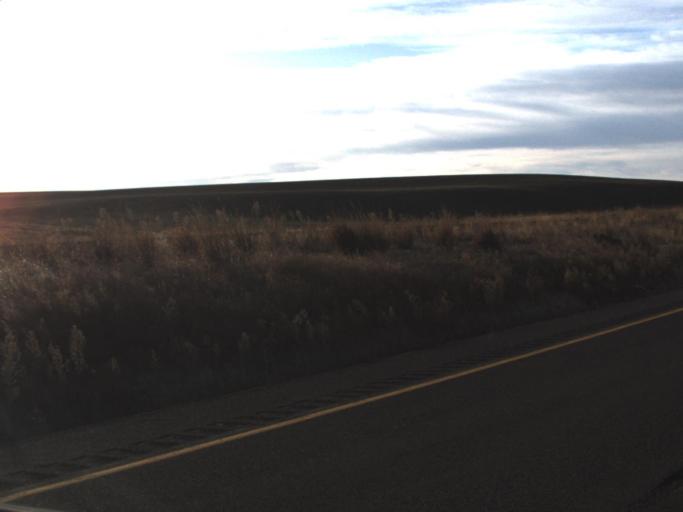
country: US
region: Washington
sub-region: Adams County
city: Ritzville
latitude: 47.0819
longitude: -118.4113
